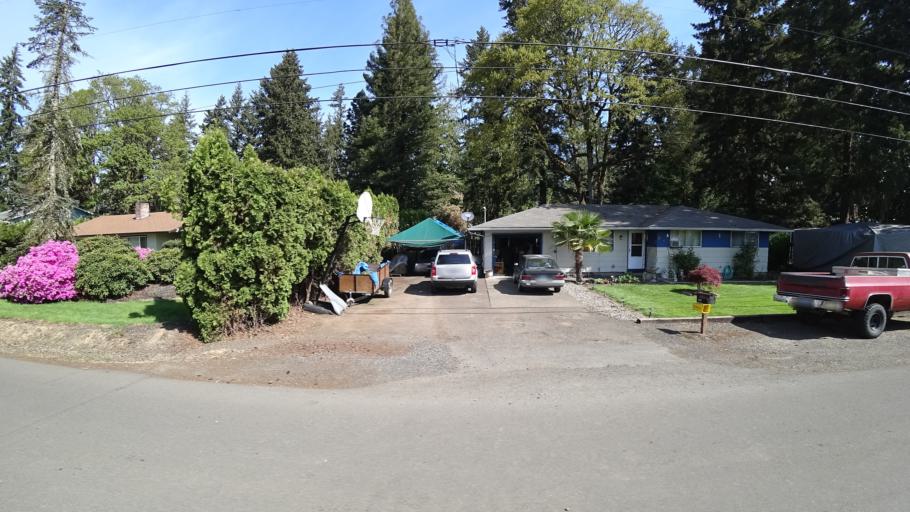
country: US
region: Oregon
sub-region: Washington County
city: Hillsboro
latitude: 45.5243
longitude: -122.9403
